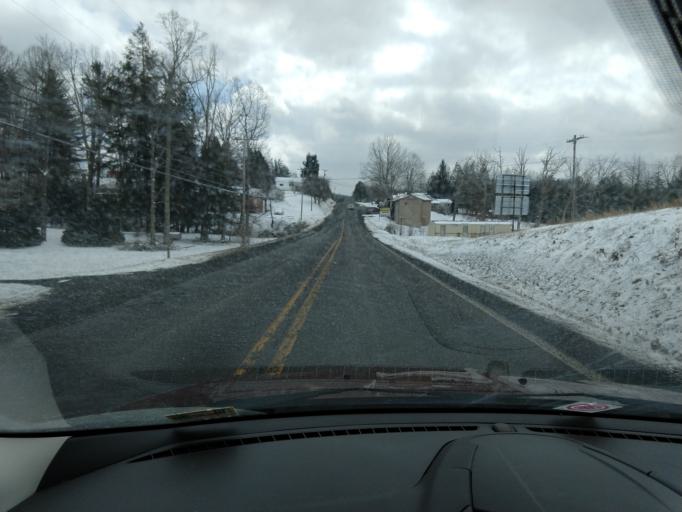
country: US
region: West Virginia
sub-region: Nicholas County
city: Craigsville
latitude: 38.3220
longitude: -80.6539
